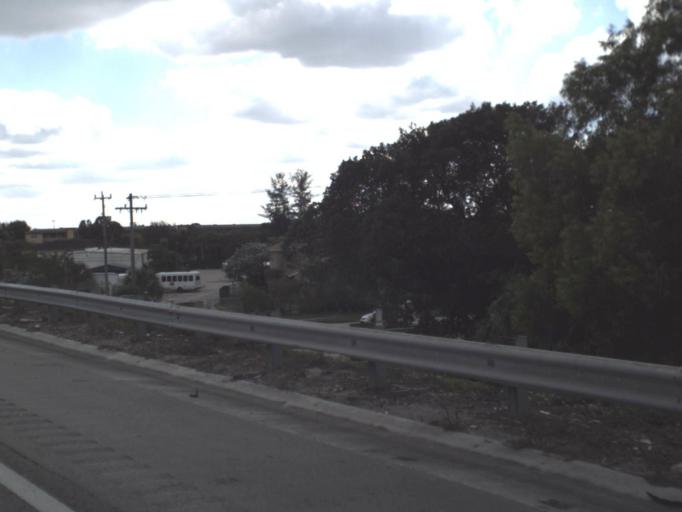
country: US
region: Florida
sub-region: Broward County
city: Coconut Creek
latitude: 26.2605
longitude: -80.1676
